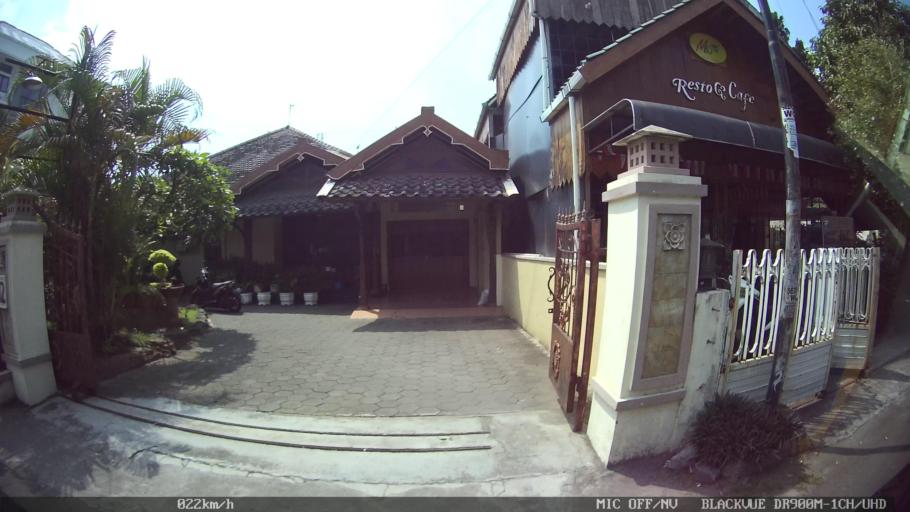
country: ID
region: Daerah Istimewa Yogyakarta
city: Yogyakarta
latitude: -7.8011
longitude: 110.3877
